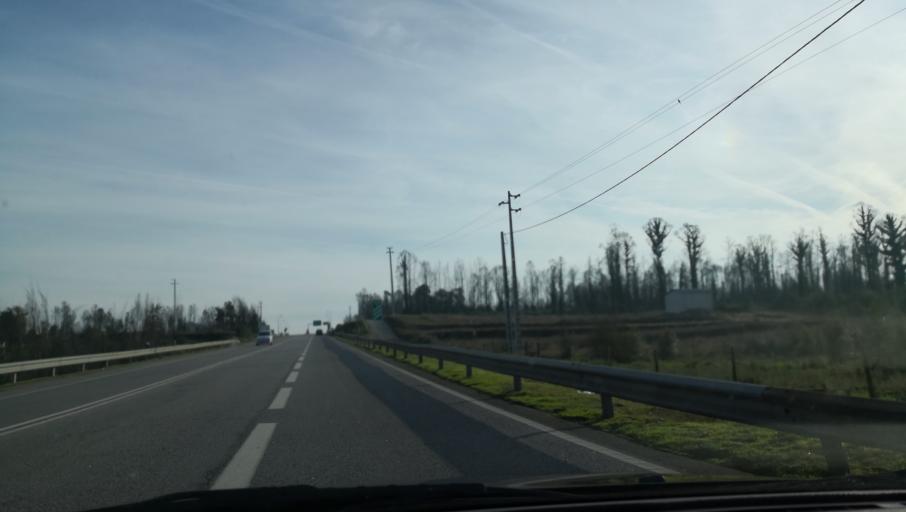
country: PT
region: Viseu
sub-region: Concelho de Tondela
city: Tondela
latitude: 40.5068
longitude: -8.0852
